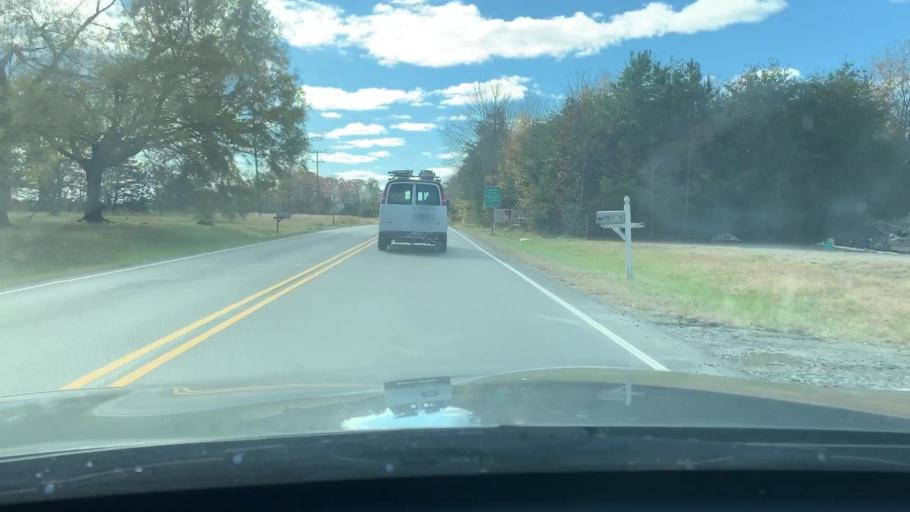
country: US
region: North Carolina
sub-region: Alamance County
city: Haw River
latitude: 36.0767
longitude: -79.3495
